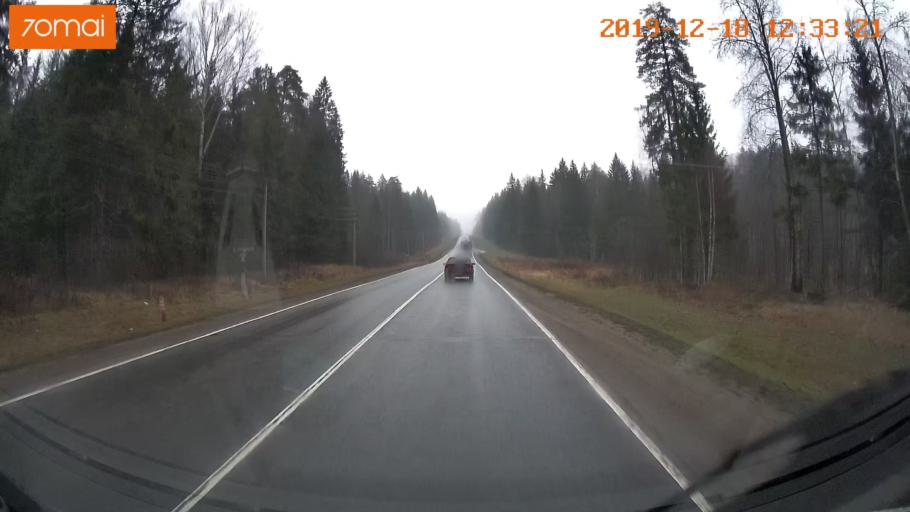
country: RU
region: Moskovskaya
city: Rumyantsevo
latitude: 56.1119
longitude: 36.5597
